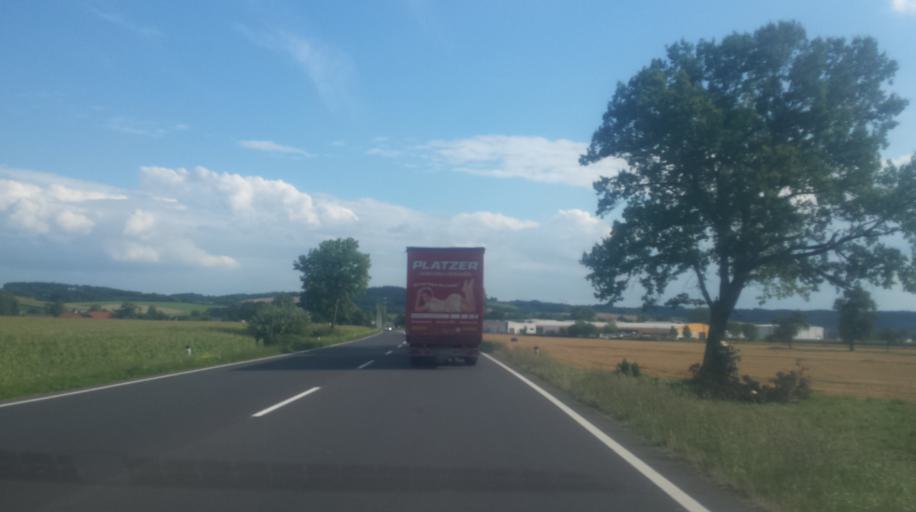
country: AT
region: Upper Austria
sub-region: Politischer Bezirk Grieskirchen
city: Bad Schallerbach
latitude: 48.2083
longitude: 13.9250
